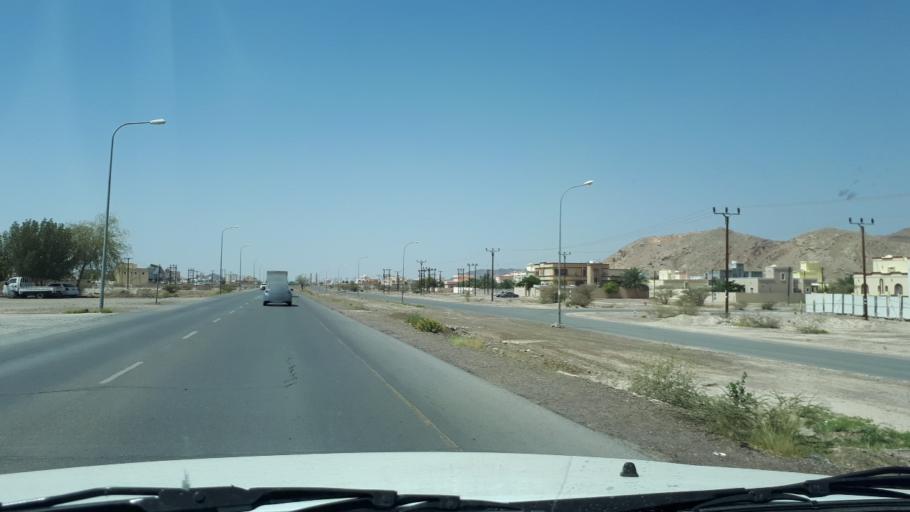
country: OM
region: Muhafazat ad Dakhiliyah
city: Bahla'
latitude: 23.0131
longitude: 57.3260
